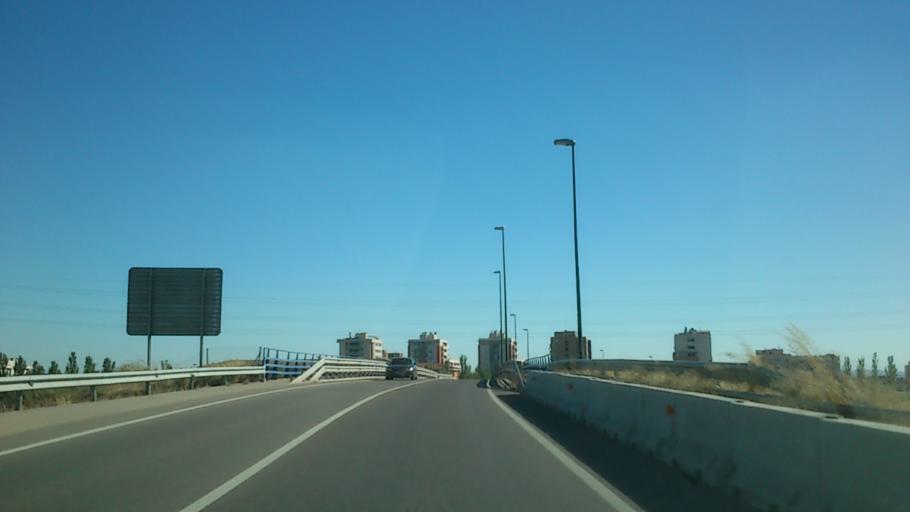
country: ES
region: Aragon
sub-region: Provincia de Zaragoza
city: Zaragoza
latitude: 41.6756
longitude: -0.8297
